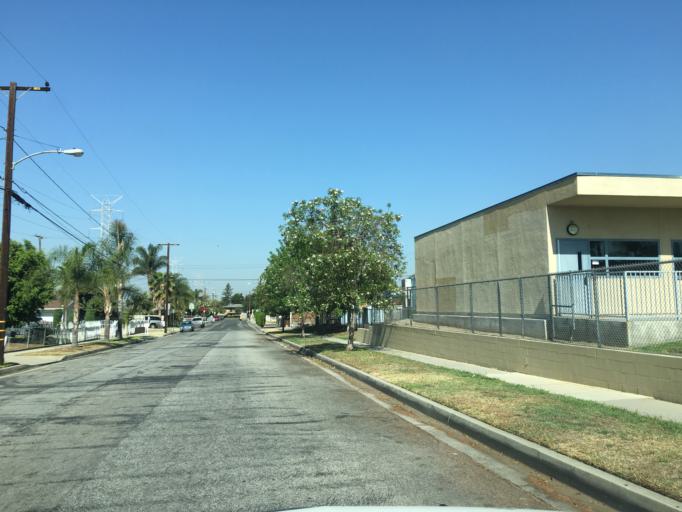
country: US
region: California
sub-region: Los Angeles County
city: Citrus
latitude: 34.1111
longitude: -117.9024
